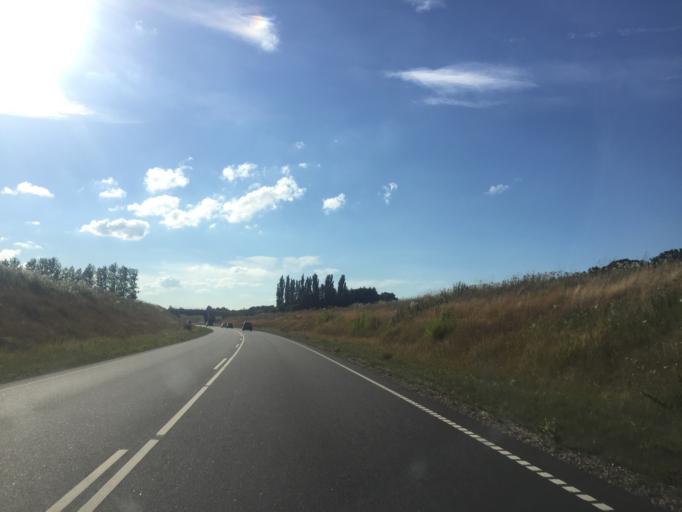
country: DK
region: Zealand
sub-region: Guldborgsund Kommune
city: Nykobing Falster
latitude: 54.7822
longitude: 11.8901
